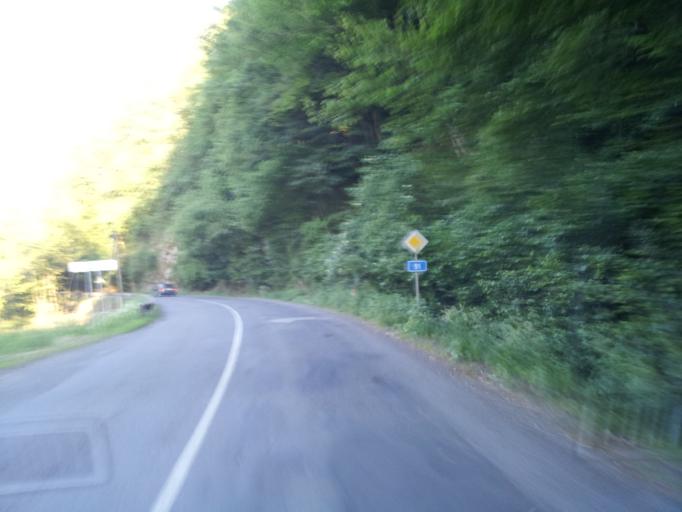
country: SK
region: Banskobystricky
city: Svaety Anton
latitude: 48.3313
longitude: 18.9673
